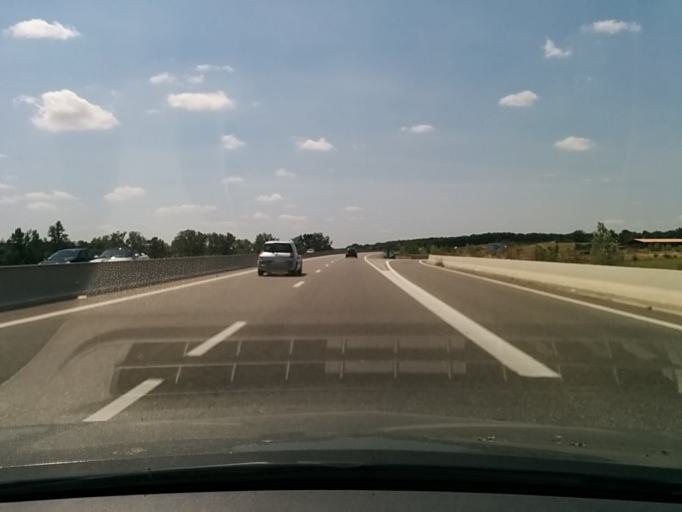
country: FR
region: Midi-Pyrenees
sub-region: Departement de la Haute-Garonne
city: La Salvetat-Saint-Gilles
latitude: 43.5893
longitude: 1.2724
